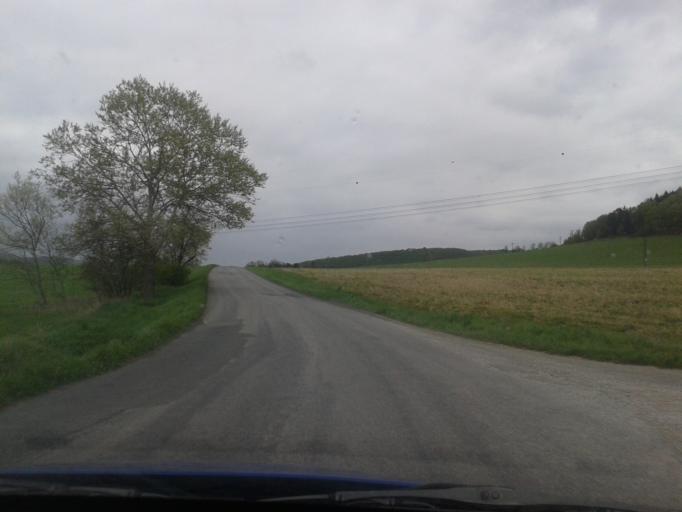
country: CZ
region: Central Bohemia
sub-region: Okres Beroun
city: Beroun
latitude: 49.9537
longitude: 14.0876
